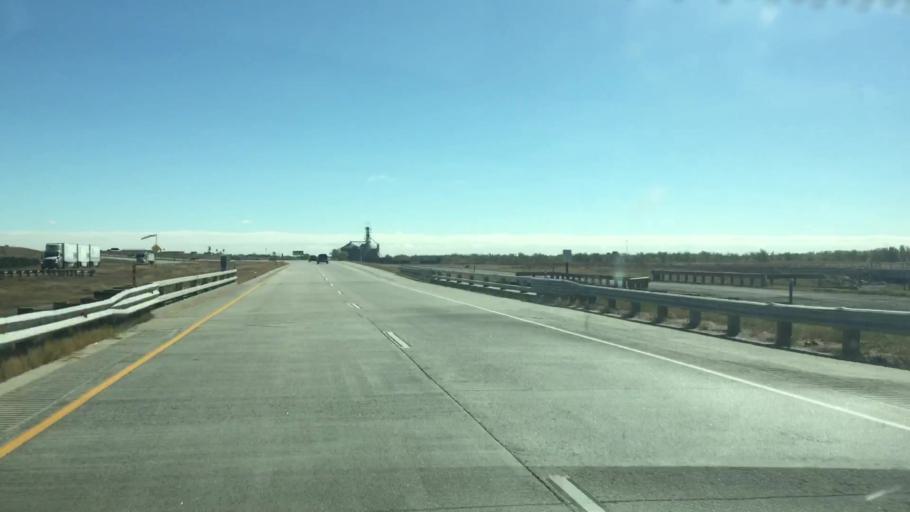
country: US
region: Colorado
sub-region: Lincoln County
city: Limon
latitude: 39.2740
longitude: -103.7394
